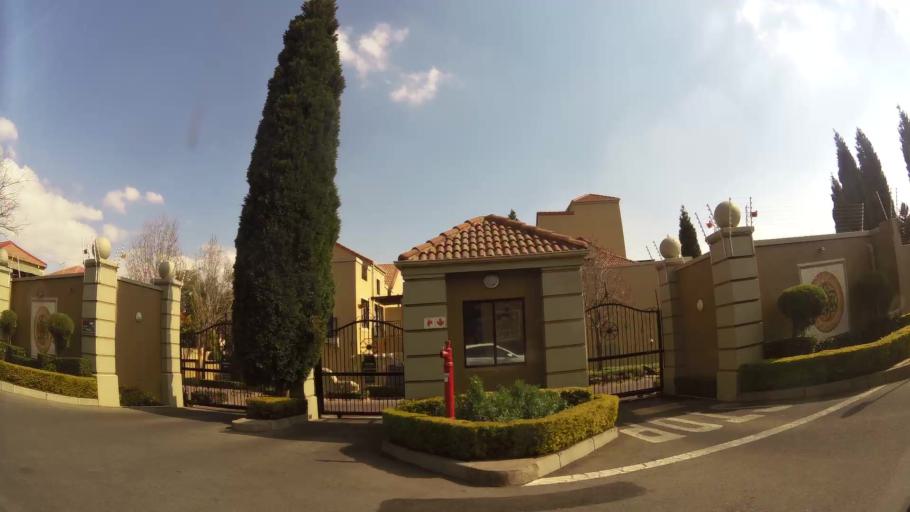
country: ZA
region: Gauteng
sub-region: City of Johannesburg Metropolitan Municipality
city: Midrand
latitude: -26.0267
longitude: 28.0671
